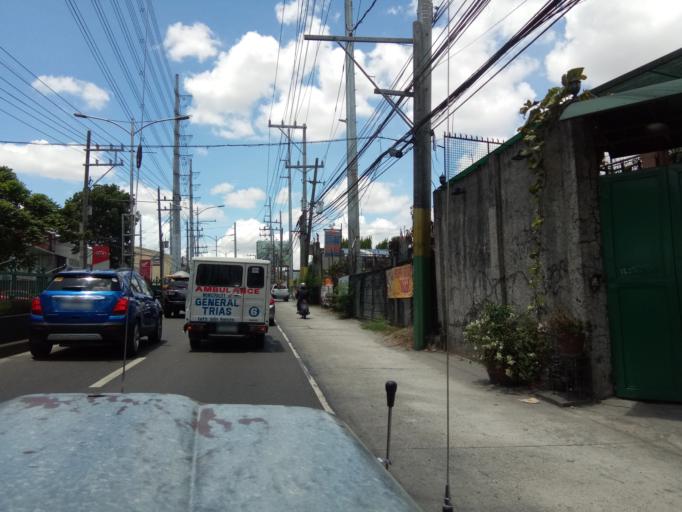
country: PH
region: Calabarzon
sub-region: Province of Cavite
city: Dasmarinas
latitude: 14.3201
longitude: 120.9424
